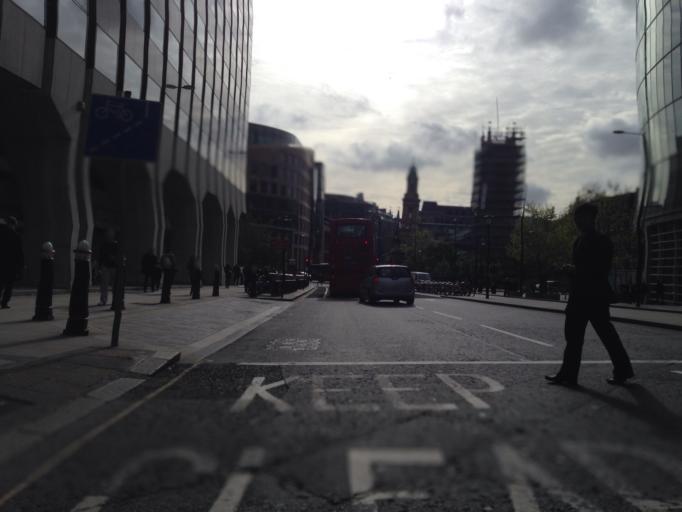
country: GB
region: England
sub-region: Greater London
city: Clerkenwell
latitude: 51.5180
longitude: -0.1092
